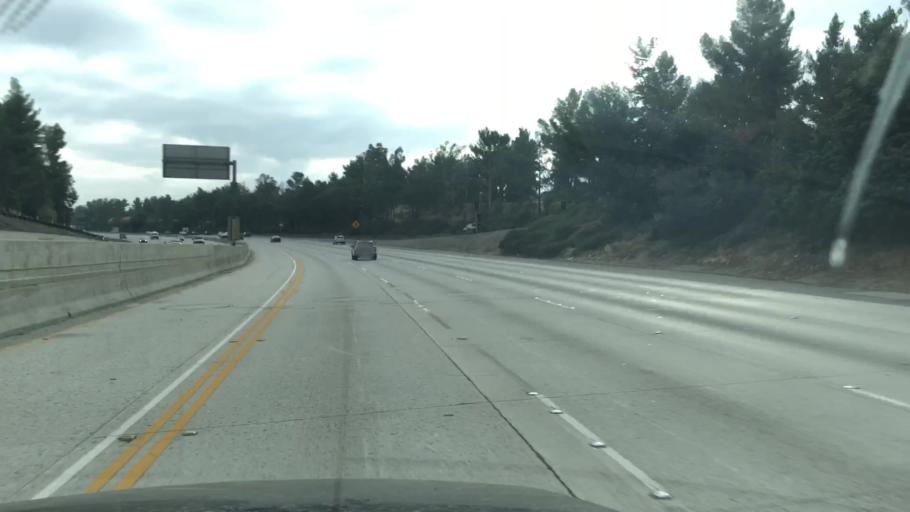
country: US
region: California
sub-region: Los Angeles County
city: Northridge
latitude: 34.2723
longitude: -118.5557
